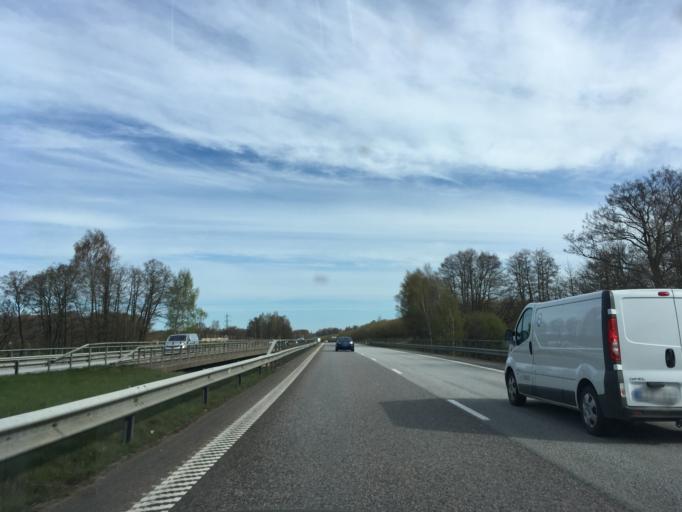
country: SE
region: Halland
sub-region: Halmstads Kommun
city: Halmstad
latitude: 56.6892
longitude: 12.8950
